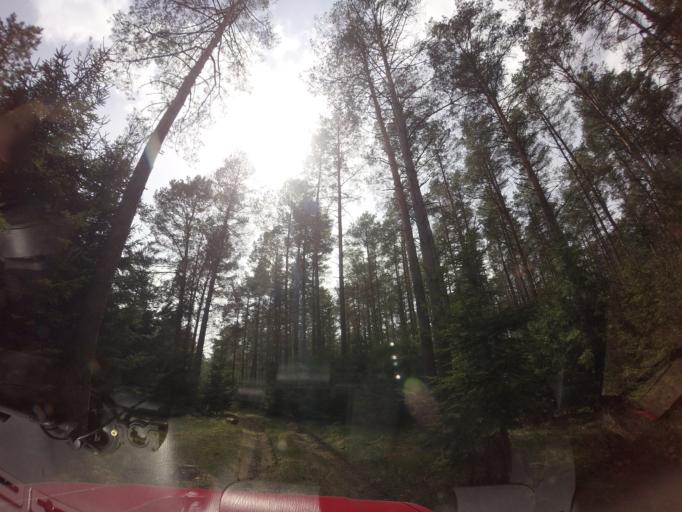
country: PL
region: West Pomeranian Voivodeship
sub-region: Powiat choszczenski
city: Drawno
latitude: 53.2766
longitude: 15.7159
